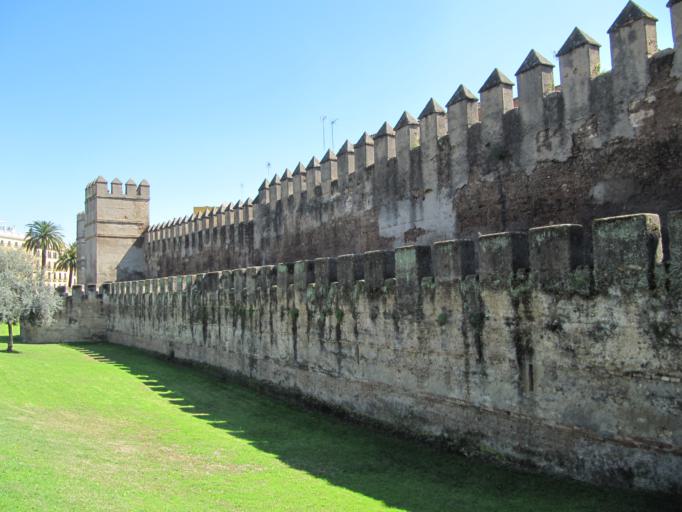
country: ES
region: Andalusia
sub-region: Provincia de Sevilla
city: Sevilla
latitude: 37.4029
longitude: -5.9888
